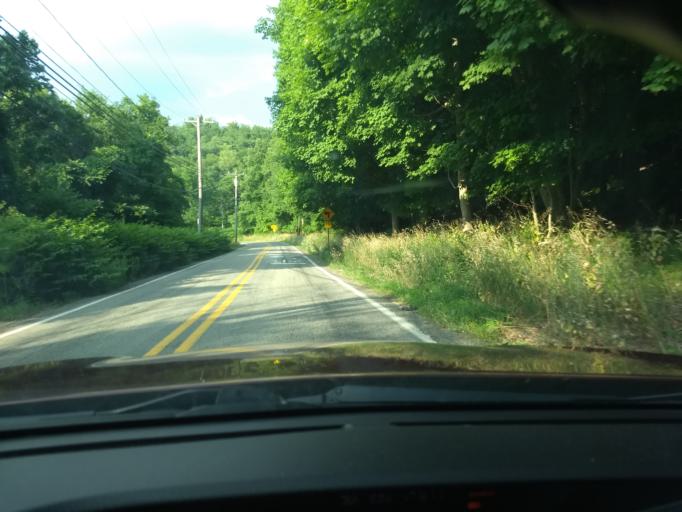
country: US
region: Pennsylvania
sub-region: Westmoreland County
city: Lower Burrell
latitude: 40.5318
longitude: -79.7547
